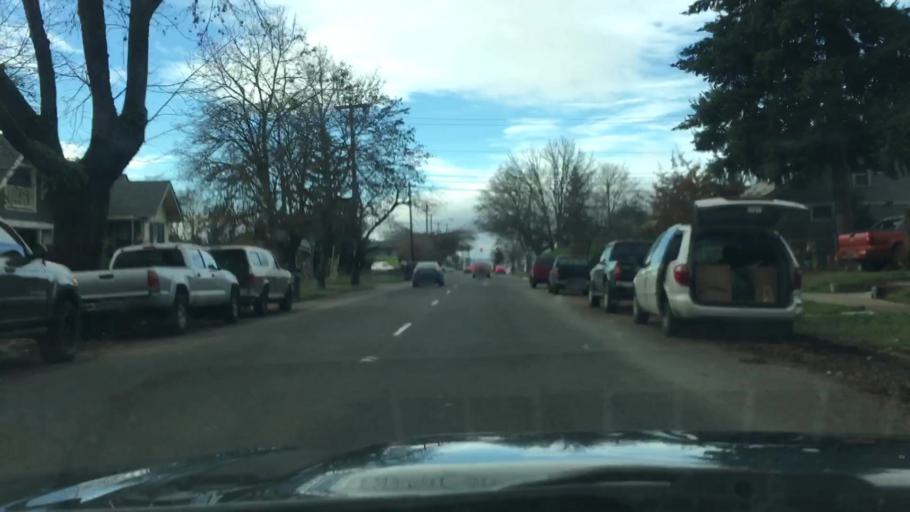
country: US
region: Oregon
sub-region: Lane County
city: Eugene
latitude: 44.0478
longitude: -123.1150
